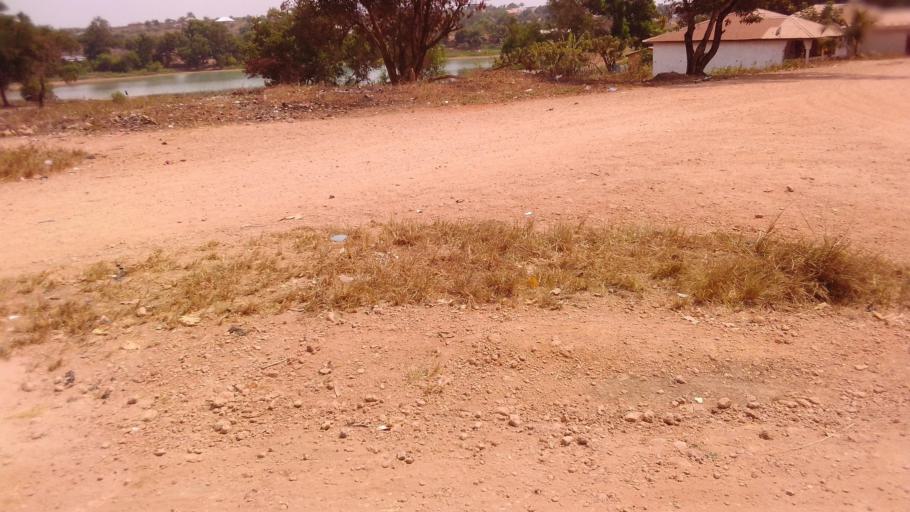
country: SL
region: Southern Province
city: Mogbwemo
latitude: 7.7961
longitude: -12.2968
